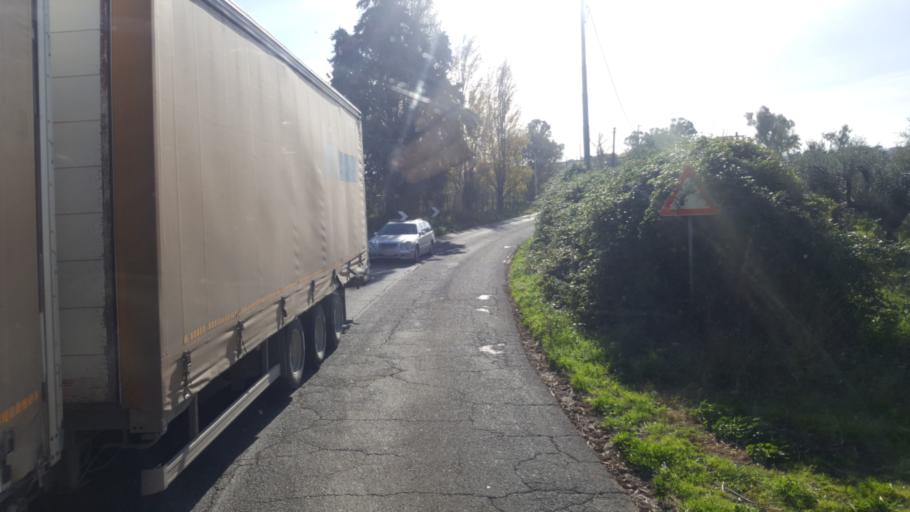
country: IT
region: Latium
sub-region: Citta metropolitana di Roma Capitale
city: Mantiglia di Ardea
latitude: 41.6619
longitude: 12.6303
